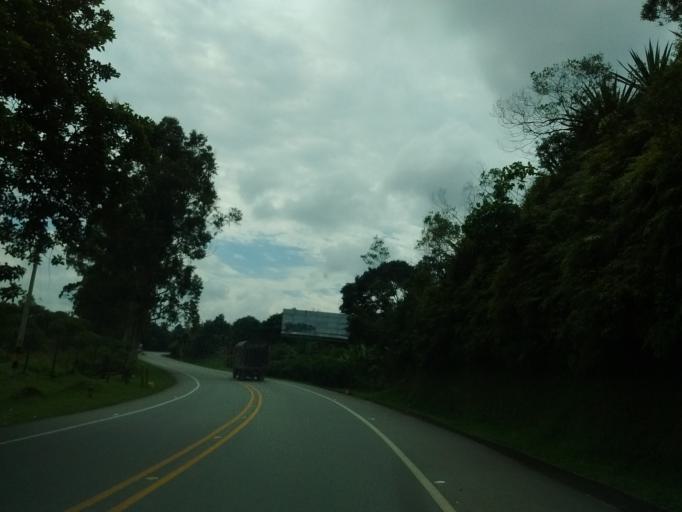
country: CO
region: Cauca
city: Cajibio
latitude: 2.5298
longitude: -76.5555
